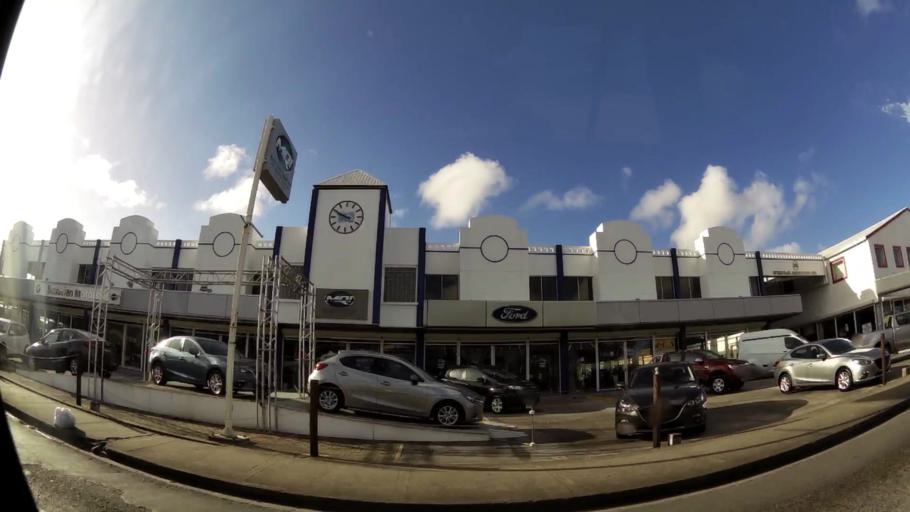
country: BB
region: Saint Michael
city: Bridgetown
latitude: 13.0908
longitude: -59.5839
